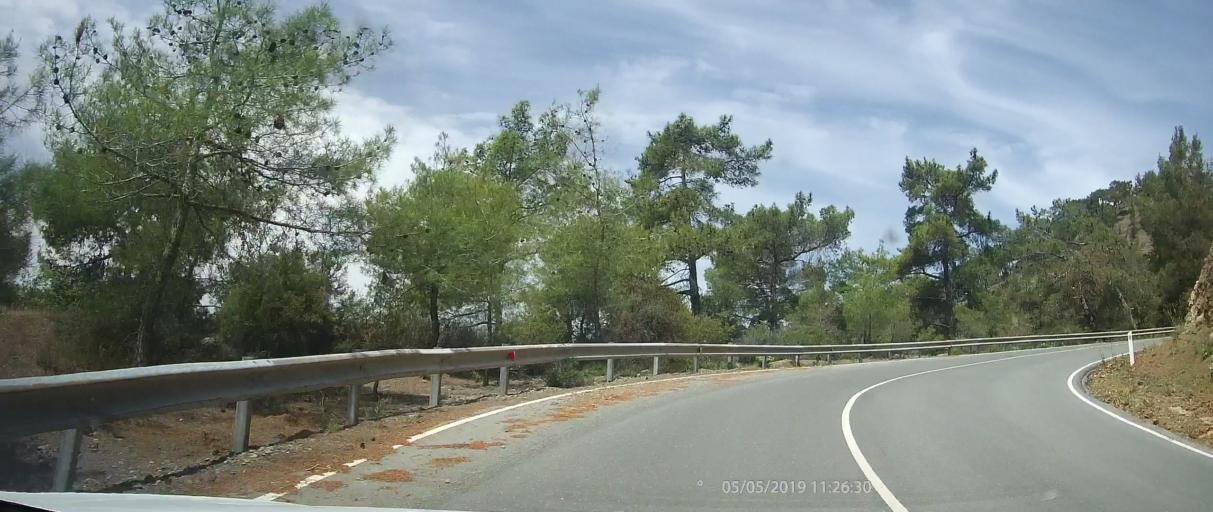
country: CY
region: Limassol
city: Pachna
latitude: 34.9291
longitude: 32.6468
